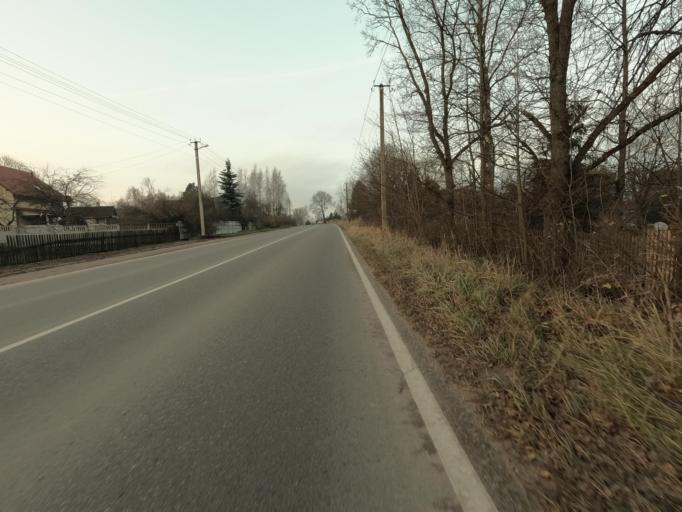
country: RU
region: Leningrad
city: Kirovsk
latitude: 59.8300
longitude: 30.9871
